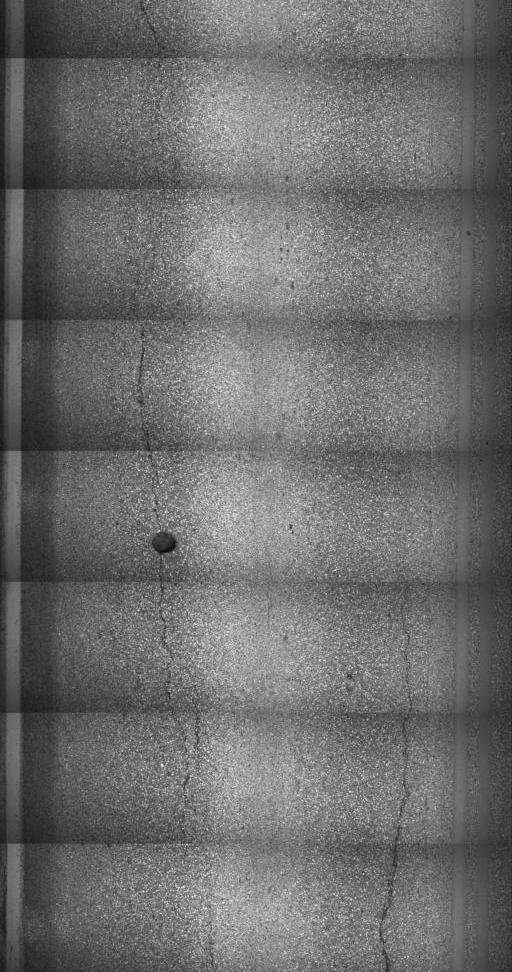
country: US
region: Vermont
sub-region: Orange County
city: Randolph
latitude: 43.7976
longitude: -72.7691
